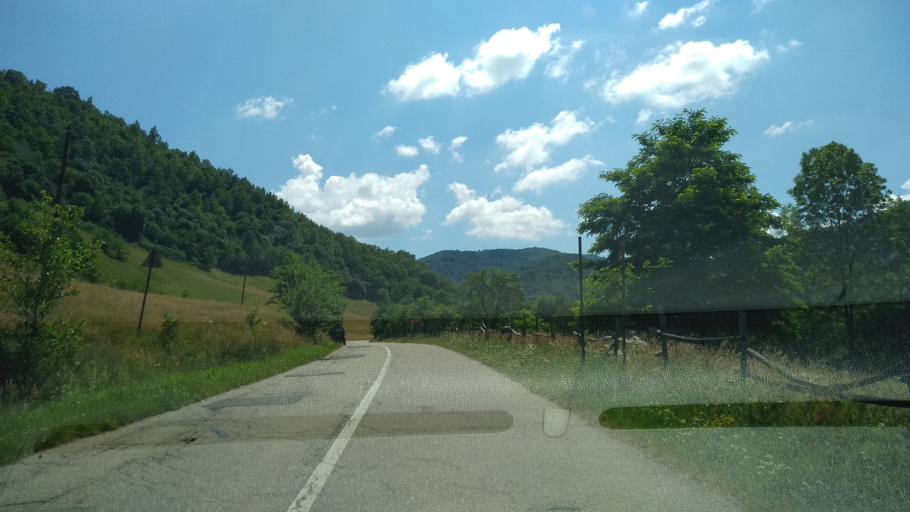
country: RO
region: Hunedoara
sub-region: Comuna Orastioara de Sus
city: Orastioara de Sus
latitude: 45.6891
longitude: 23.1621
